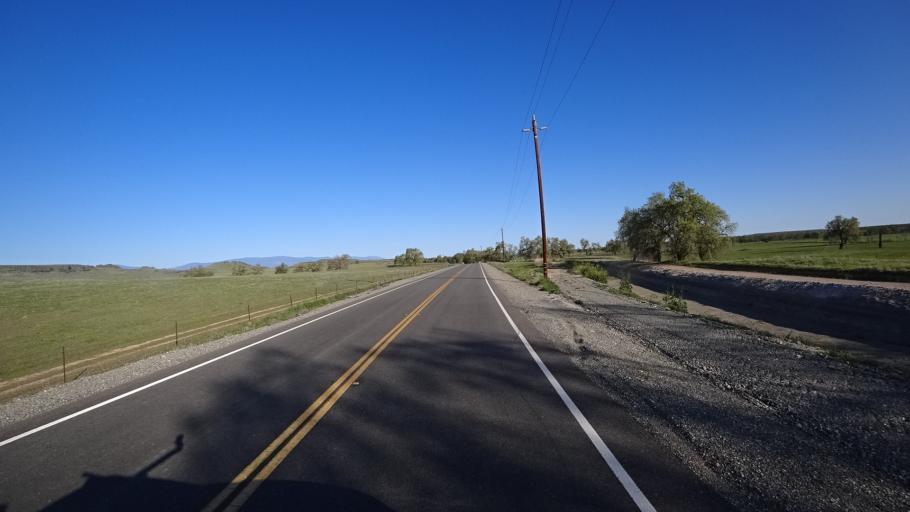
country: US
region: California
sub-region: Glenn County
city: Orland
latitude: 39.7902
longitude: -122.3101
